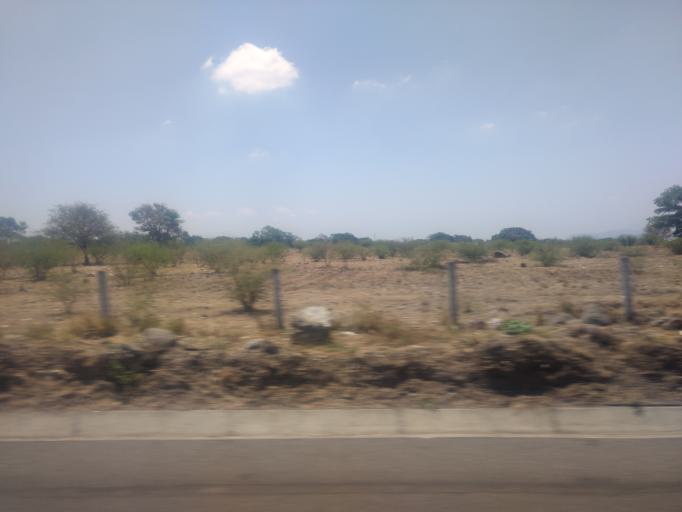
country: MX
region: Colima
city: Cuauhtemoc
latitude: 19.3469
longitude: -103.5672
